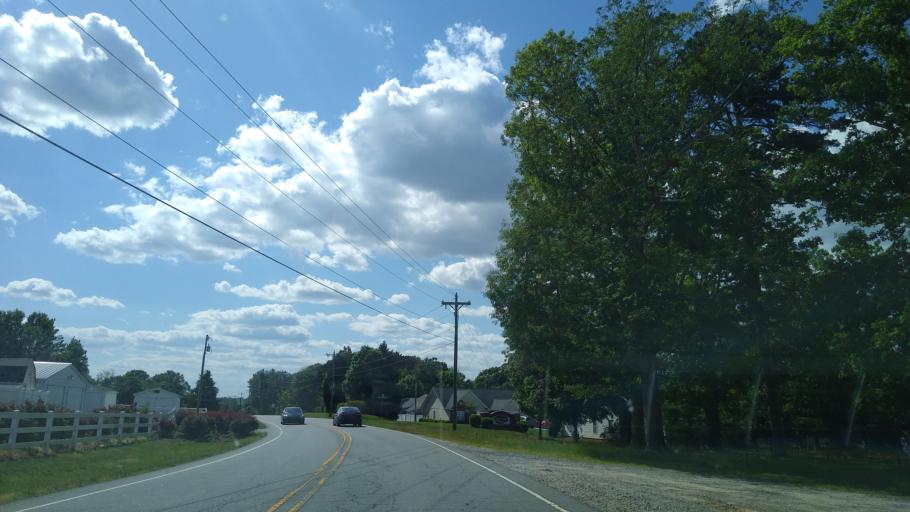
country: US
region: North Carolina
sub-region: Forsyth County
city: Kernersville
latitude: 36.1011
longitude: -80.0877
